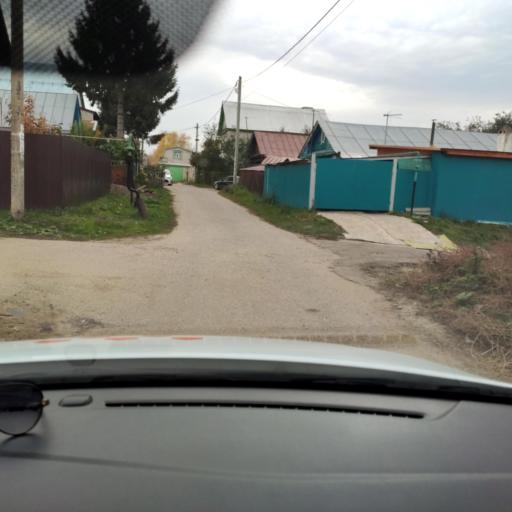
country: RU
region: Tatarstan
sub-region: Gorod Kazan'
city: Kazan
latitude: 55.7494
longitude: 49.1765
